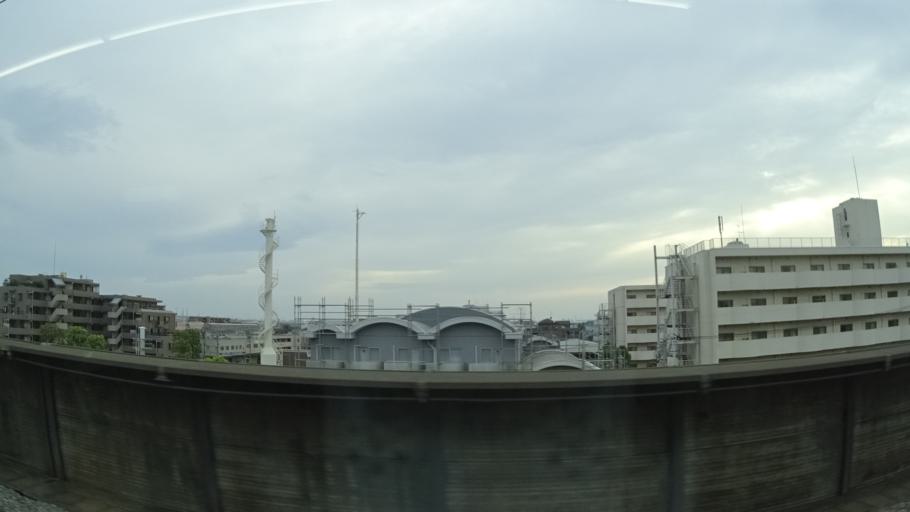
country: JP
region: Saitama
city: Shimotoda
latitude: 35.8368
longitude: 139.6515
